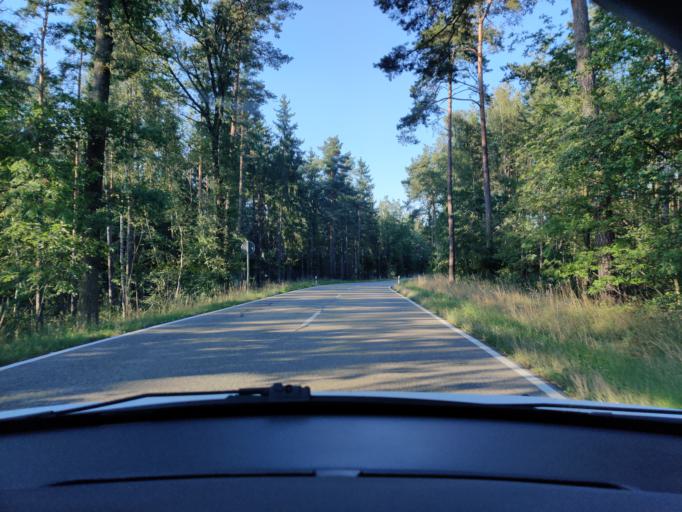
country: DE
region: Bavaria
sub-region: Upper Palatinate
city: Stulln
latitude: 49.4319
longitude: 12.1429
